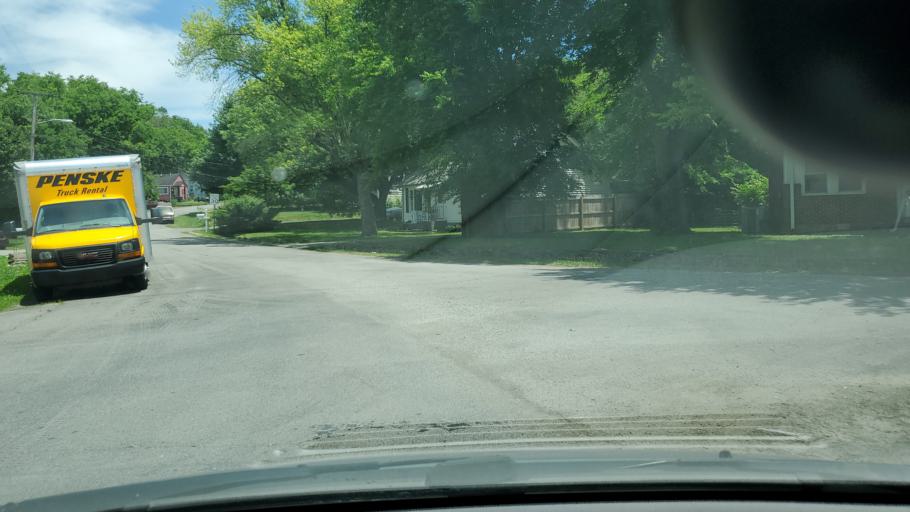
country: US
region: Tennessee
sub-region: Davidson County
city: Nashville
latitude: 36.2061
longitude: -86.7575
